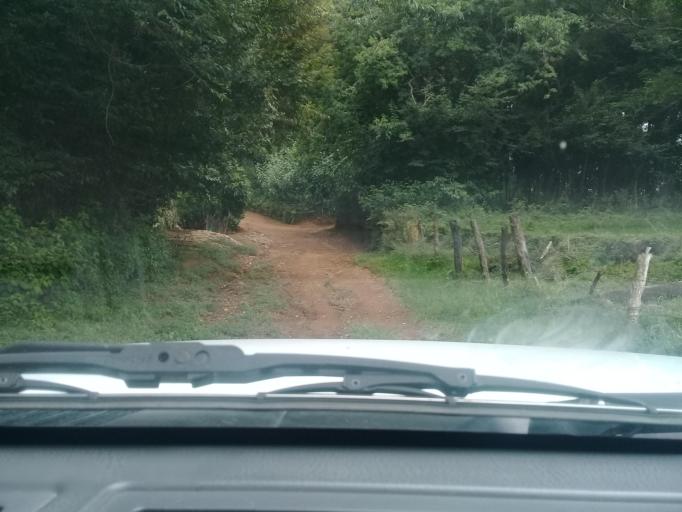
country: MX
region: Veracruz
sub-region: Tlalnelhuayocan
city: Otilpan
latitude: 19.5480
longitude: -96.9776
